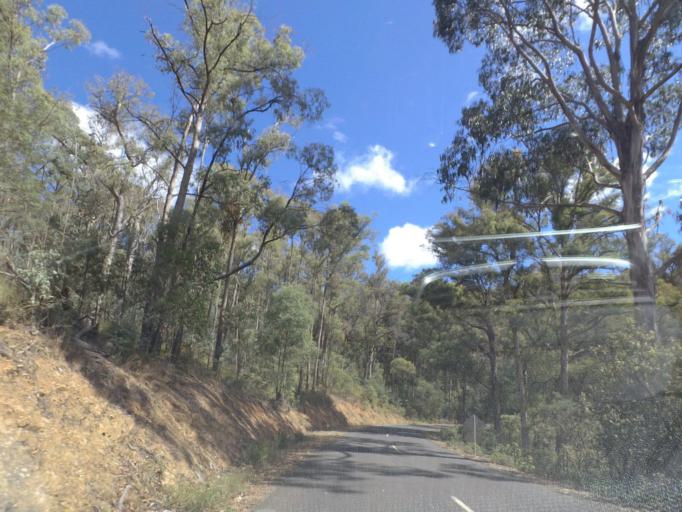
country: AU
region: Victoria
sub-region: Murrindindi
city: Alexandra
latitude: -37.3304
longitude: 145.9436
